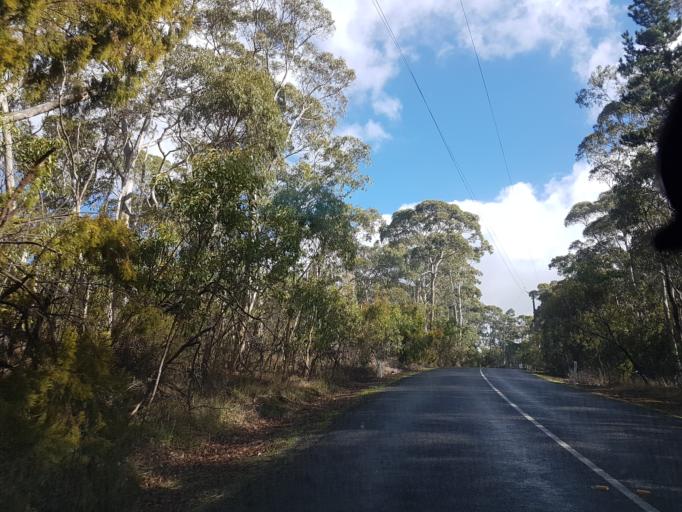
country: AU
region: South Australia
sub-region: Adelaide Hills
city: Heathfield
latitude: -35.0453
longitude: 138.7027
